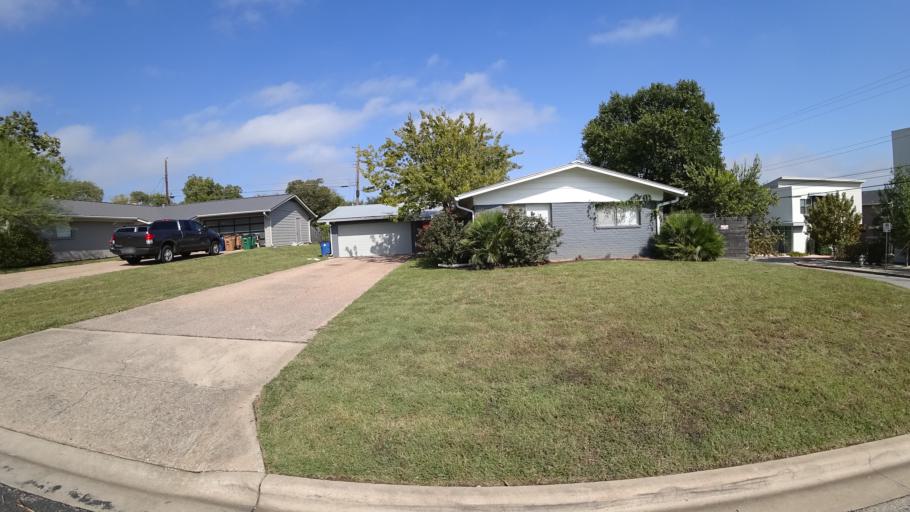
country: US
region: Texas
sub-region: Travis County
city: Rollingwood
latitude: 30.2497
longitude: -97.7730
